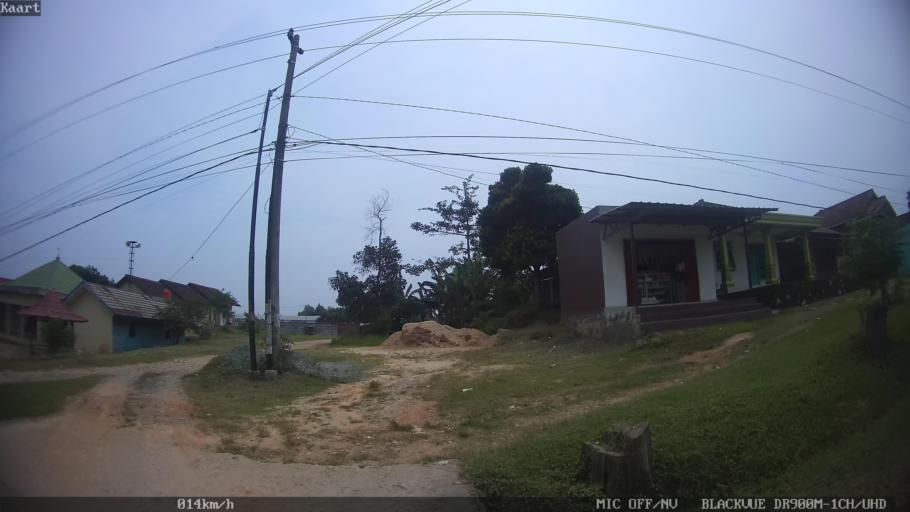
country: ID
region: Lampung
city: Bandarlampung
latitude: -5.4065
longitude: 105.3063
